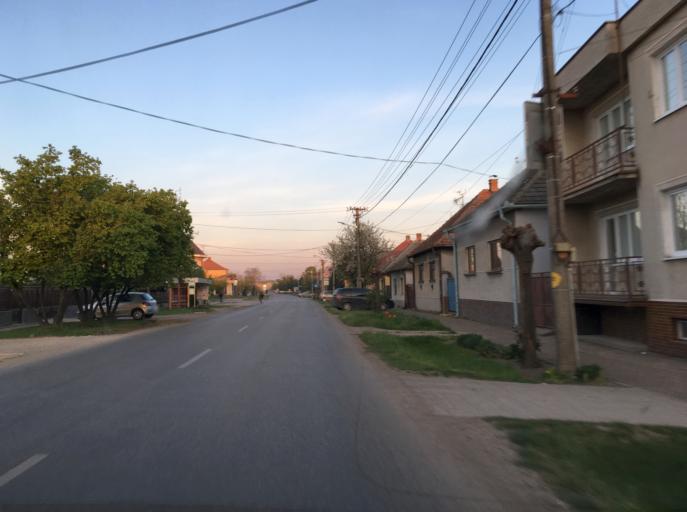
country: SK
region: Nitriansky
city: Kolarovo
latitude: 47.9112
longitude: 18.0027
